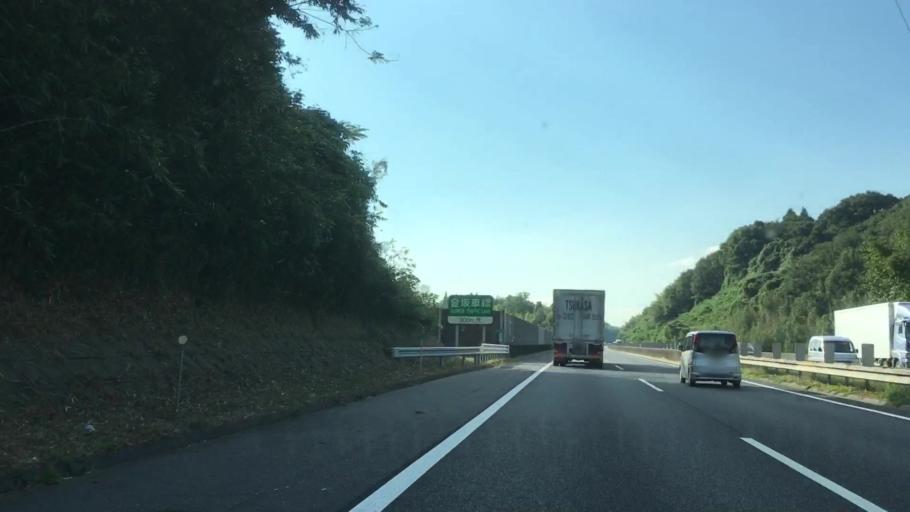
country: JP
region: Yamaguchi
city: Hikari
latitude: 34.0285
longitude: 131.9459
